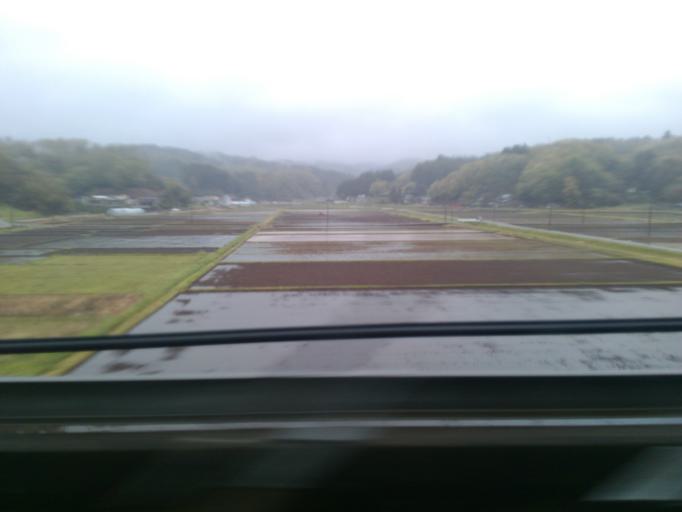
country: JP
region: Miyagi
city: Okawara
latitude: 38.0573
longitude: 140.7087
